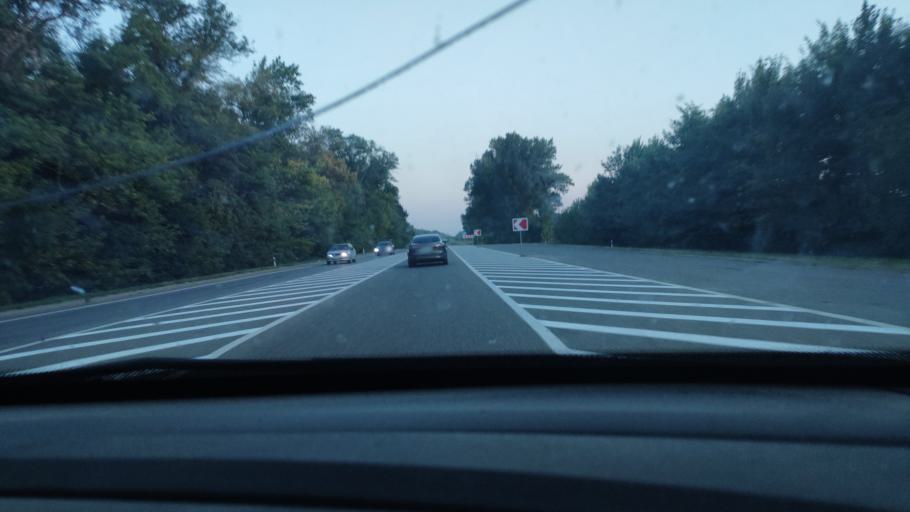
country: RU
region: Krasnodarskiy
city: Medvedovskaya
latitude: 45.4605
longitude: 38.9857
